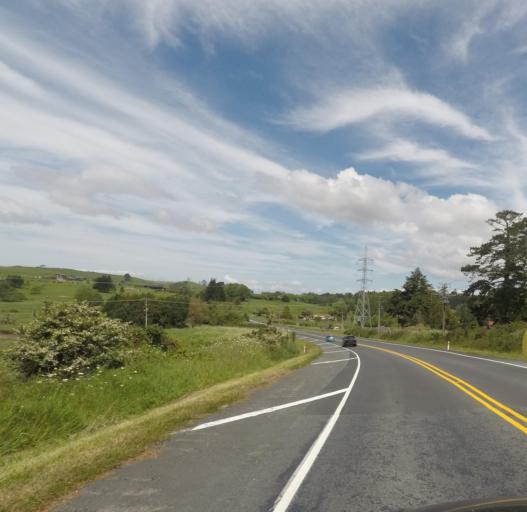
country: NZ
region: Auckland
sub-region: Auckland
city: Rothesay Bay
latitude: -36.6601
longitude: 174.6714
